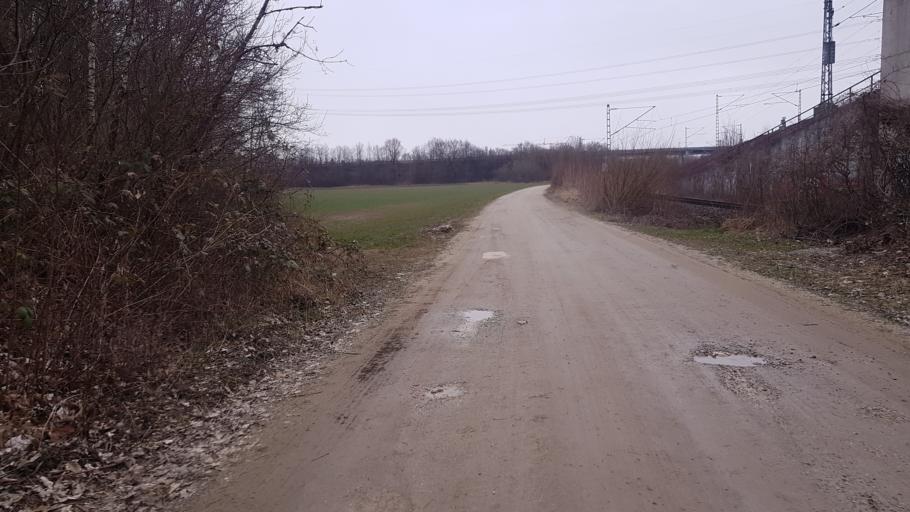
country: DE
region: Bavaria
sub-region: Upper Bavaria
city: Unterfoehring
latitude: 48.1798
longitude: 11.6447
